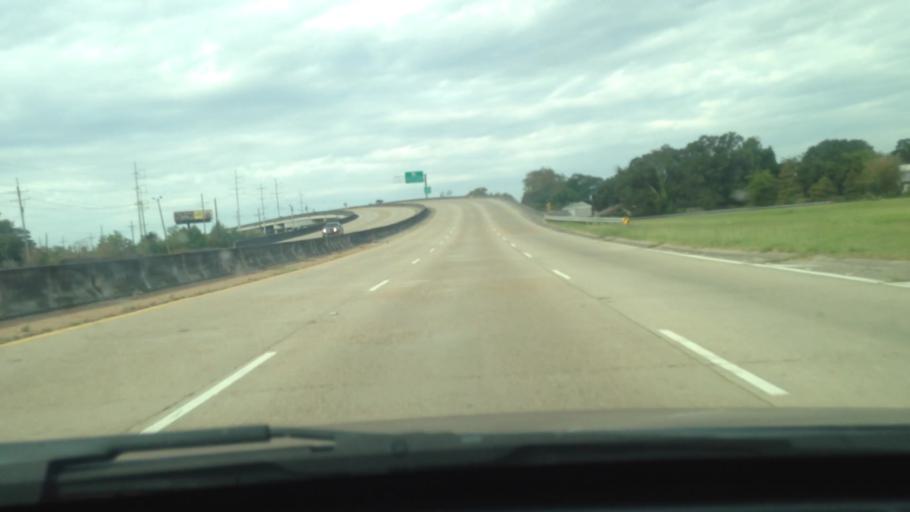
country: US
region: Louisiana
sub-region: Jefferson Parish
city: Metairie Terrace
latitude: 29.9715
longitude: -90.1685
